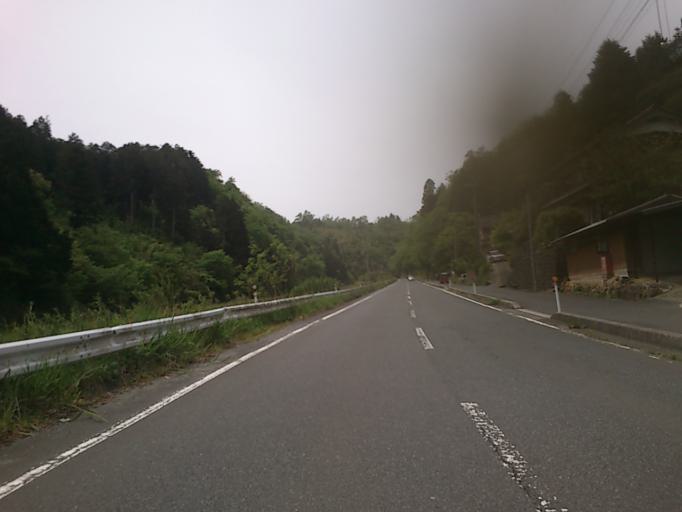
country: JP
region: Kyoto
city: Miyazu
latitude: 35.5909
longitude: 135.1304
